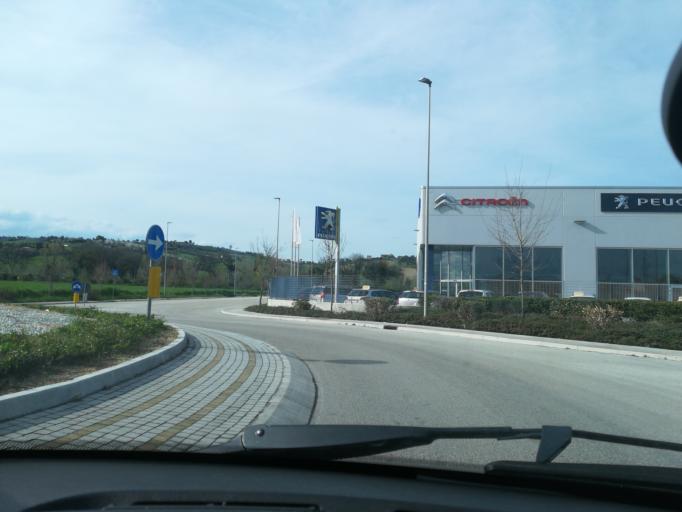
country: IT
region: The Marches
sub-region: Provincia di Macerata
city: Piediripa
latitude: 43.2829
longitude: 13.4971
